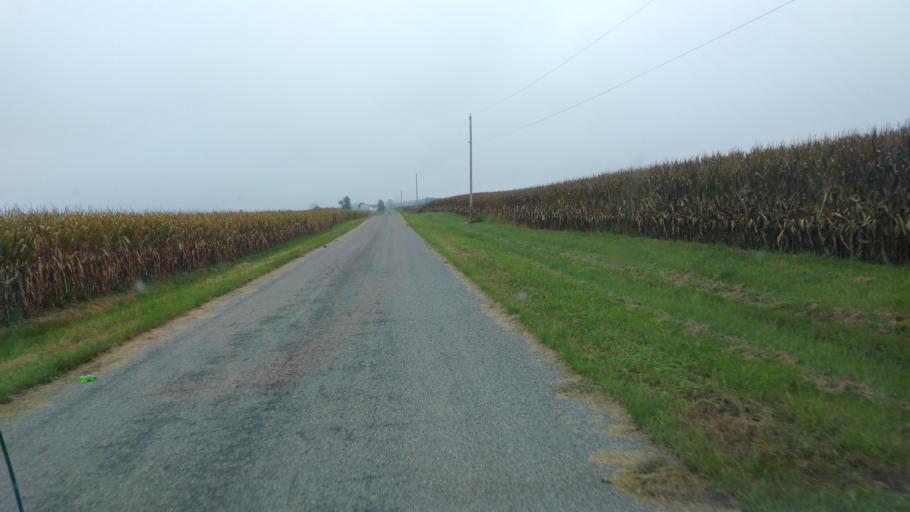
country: US
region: Ohio
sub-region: Hardin County
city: Kenton
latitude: 40.5129
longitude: -83.5996
